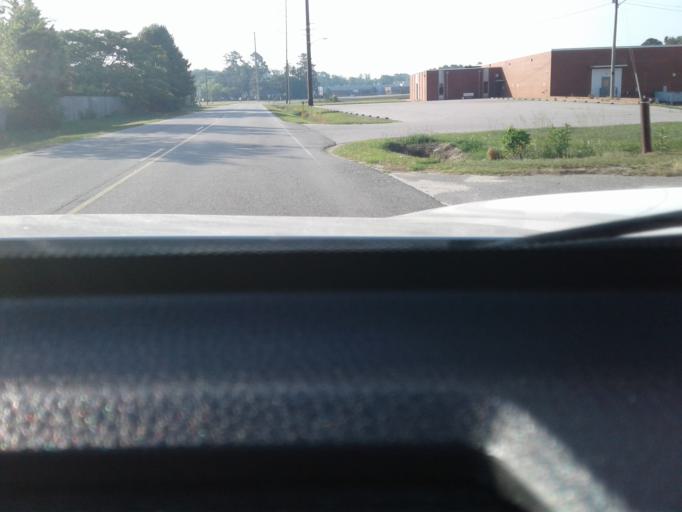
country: US
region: North Carolina
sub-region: Harnett County
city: Dunn
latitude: 35.3230
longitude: -78.6243
